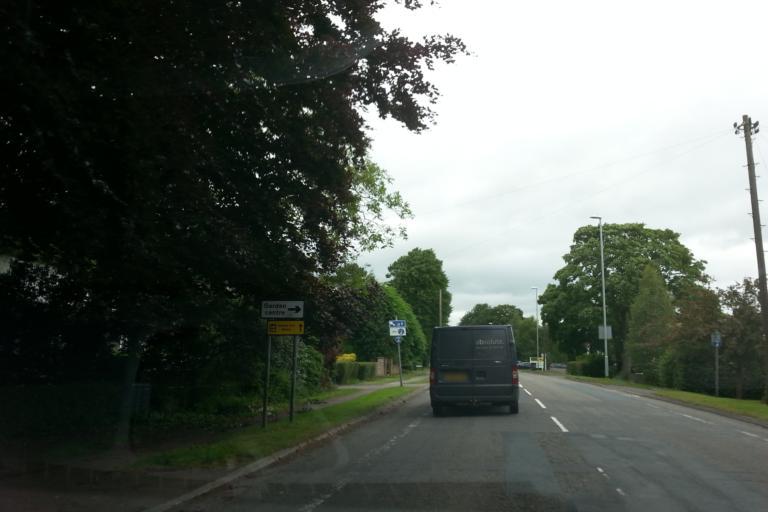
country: GB
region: England
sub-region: Cambridgeshire
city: Cambridge
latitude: 52.1591
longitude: 0.1269
